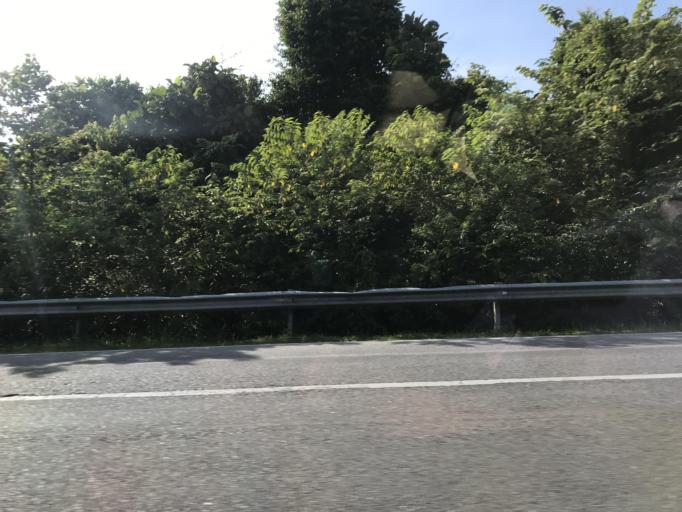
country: MY
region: Kelantan
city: Peringat
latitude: 6.0566
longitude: 102.2277
